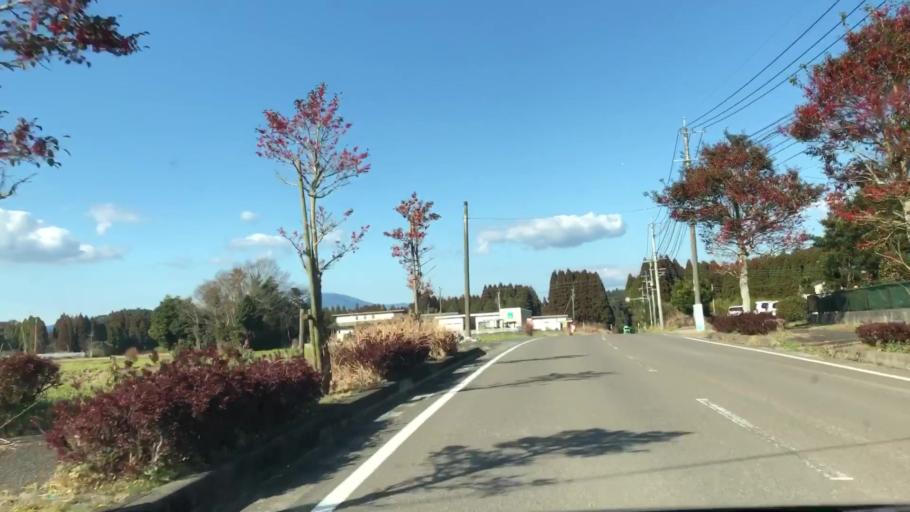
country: JP
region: Kagoshima
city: Satsumasendai
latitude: 31.8377
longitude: 130.4299
